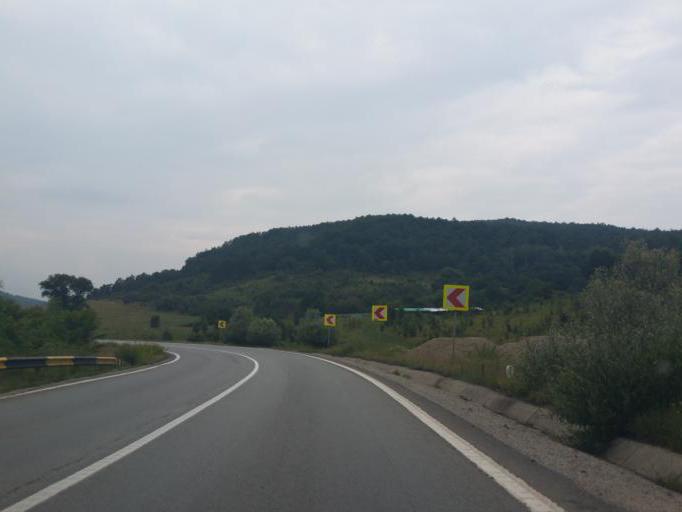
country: RO
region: Salaj
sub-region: Comuna Zimbor
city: Zimbor
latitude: 46.9688
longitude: 23.2775
